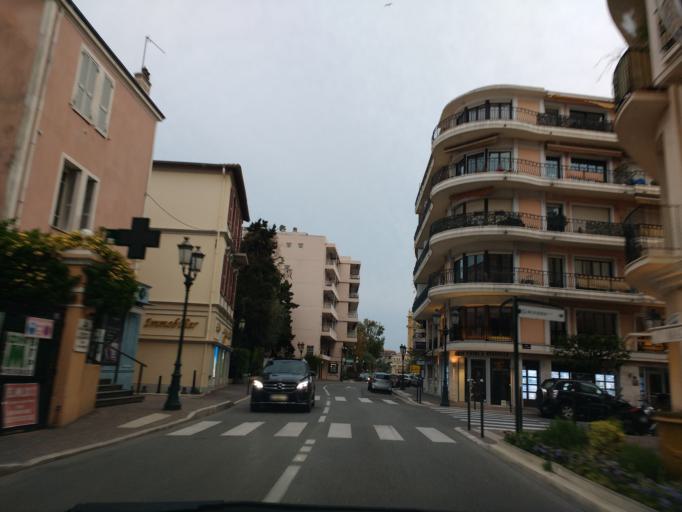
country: FR
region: Provence-Alpes-Cote d'Azur
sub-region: Departement des Alpes-Maritimes
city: Beaulieu-sur-Mer
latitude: 43.7057
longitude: 7.3345
